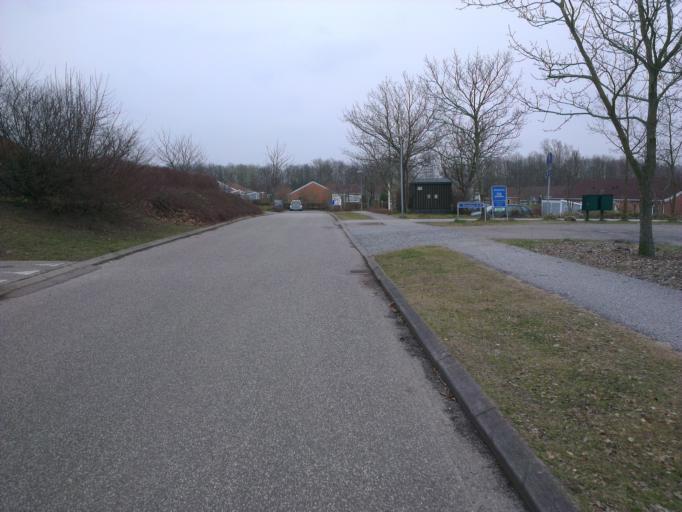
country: DK
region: Capital Region
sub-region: Frederikssund Kommune
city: Frederikssund
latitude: 55.8599
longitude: 12.0805
